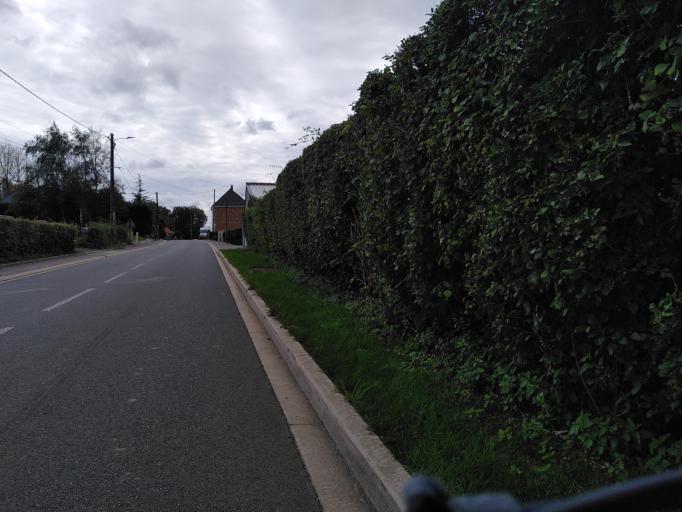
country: FR
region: Nord-Pas-de-Calais
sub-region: Departement du Pas-de-Calais
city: Longfosse
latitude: 50.6950
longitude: 1.7880
